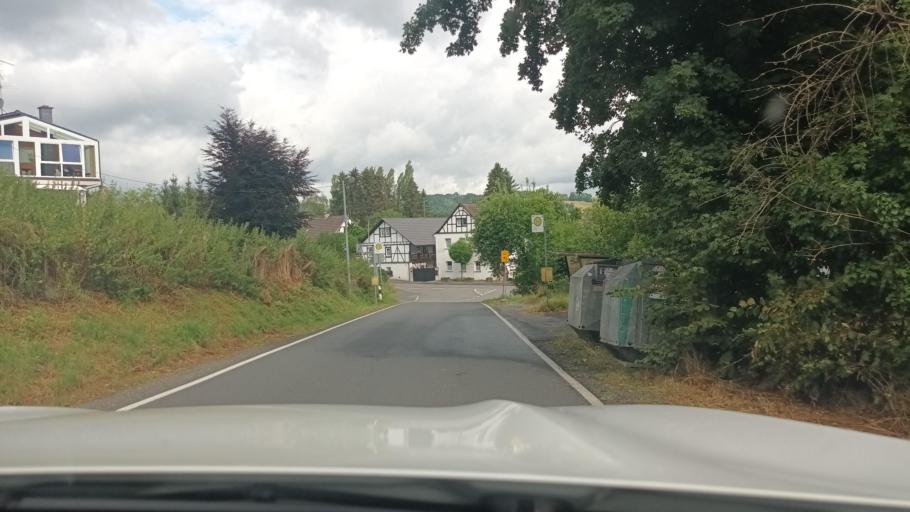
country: DE
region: North Rhine-Westphalia
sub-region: Regierungsbezirk Koln
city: Hennef
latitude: 50.7643
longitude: 7.3559
